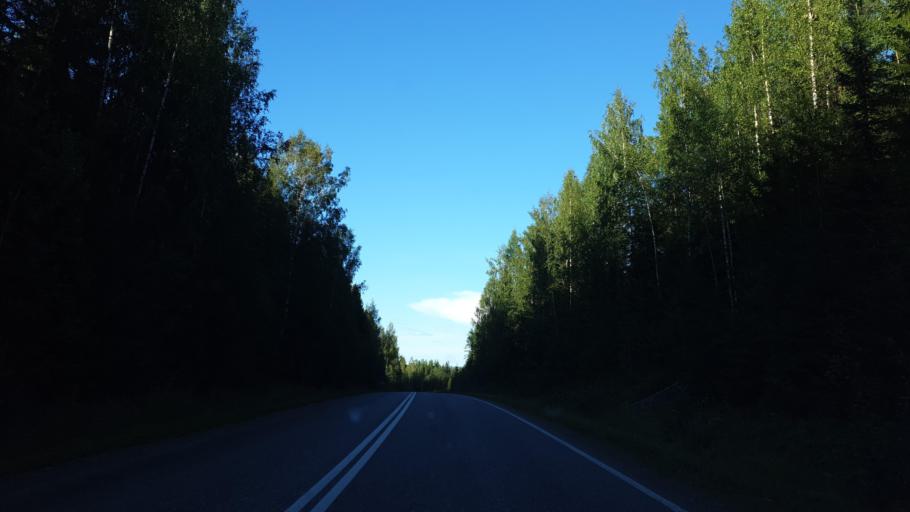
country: FI
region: Northern Savo
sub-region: Koillis-Savo
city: Juankoski
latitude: 63.0996
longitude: 28.4338
